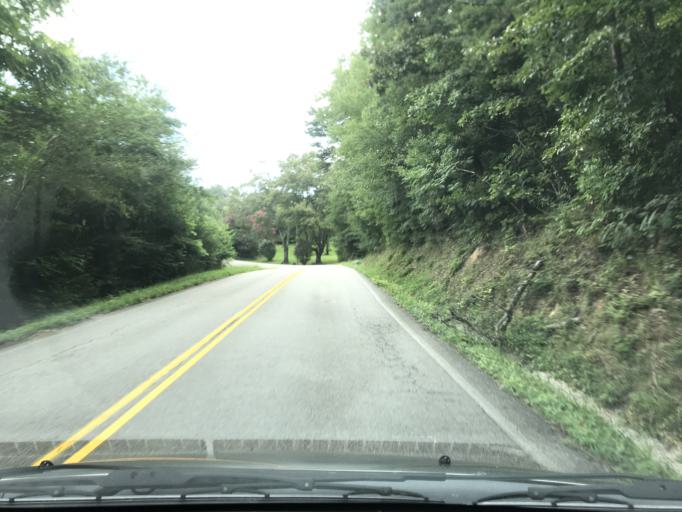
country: US
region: Tennessee
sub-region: Hamilton County
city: Lakesite
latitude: 35.1684
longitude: -85.0842
